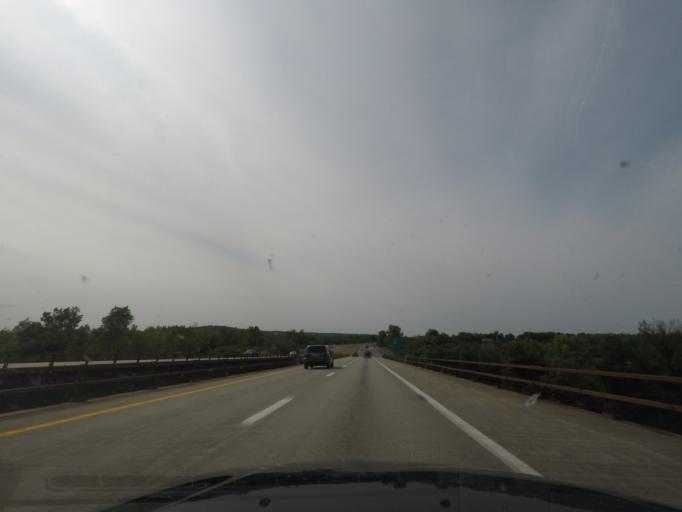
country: US
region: New York
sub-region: Essex County
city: Keeseville
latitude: 44.4908
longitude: -73.4937
